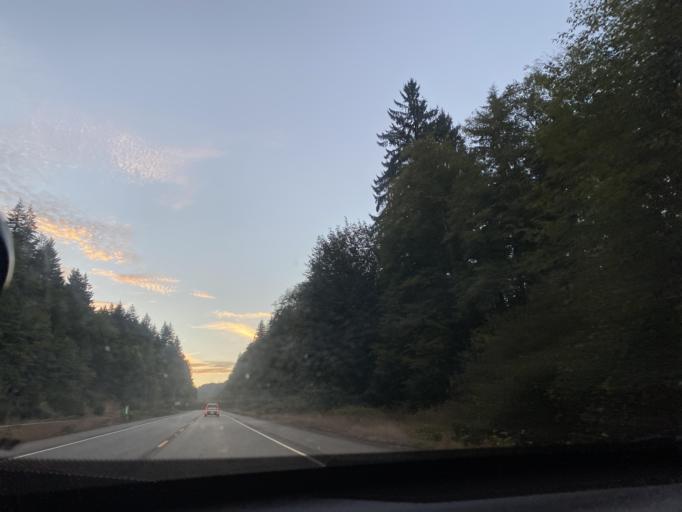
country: US
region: Washington
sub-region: Clallam County
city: Port Angeles
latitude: 48.0697
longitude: -123.6282
